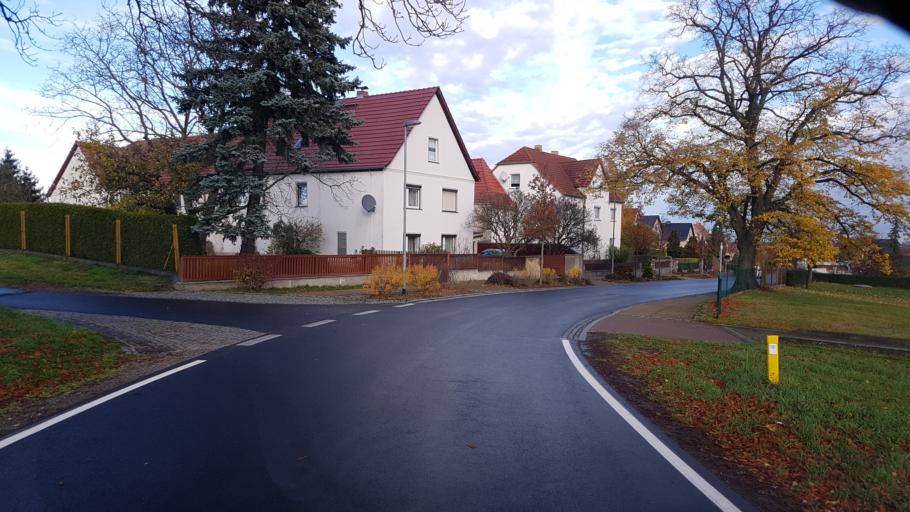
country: DE
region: Brandenburg
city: Ortrand
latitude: 51.3392
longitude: 13.7640
